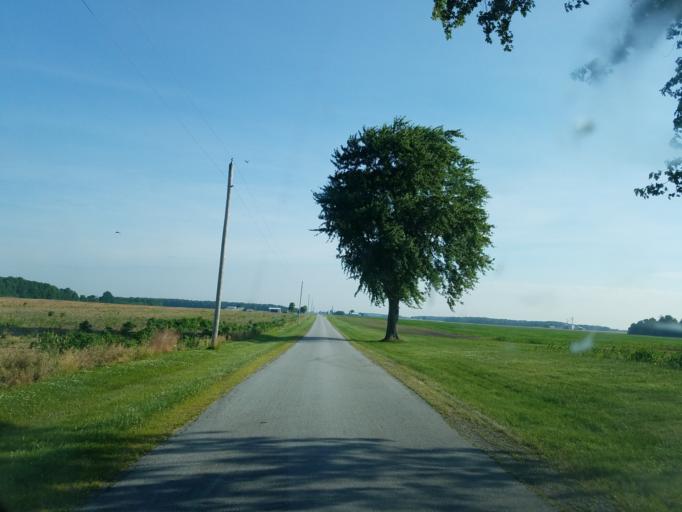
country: US
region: Ohio
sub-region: Hardin County
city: Kenton
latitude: 40.7343
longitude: -83.6717
